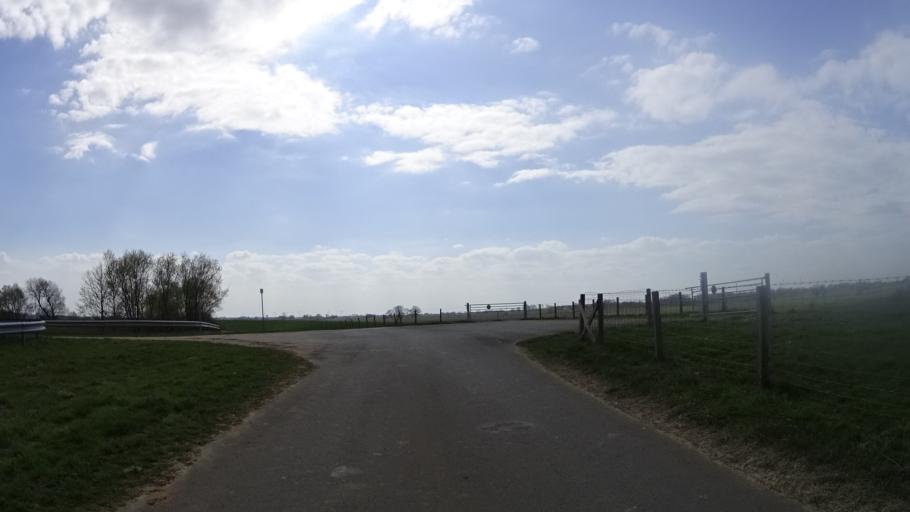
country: DE
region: Lower Saxony
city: Rhede
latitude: 53.0945
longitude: 7.2981
